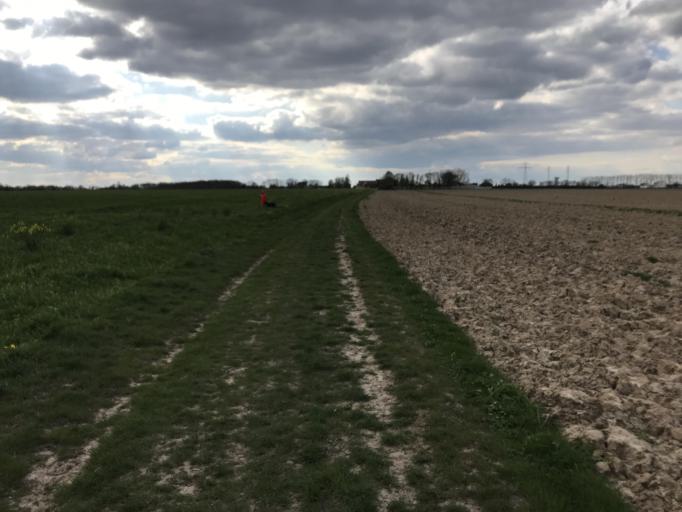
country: FR
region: Ile-de-France
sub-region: Departement de l'Essonne
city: Vauhallan
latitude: 48.7407
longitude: 2.2098
